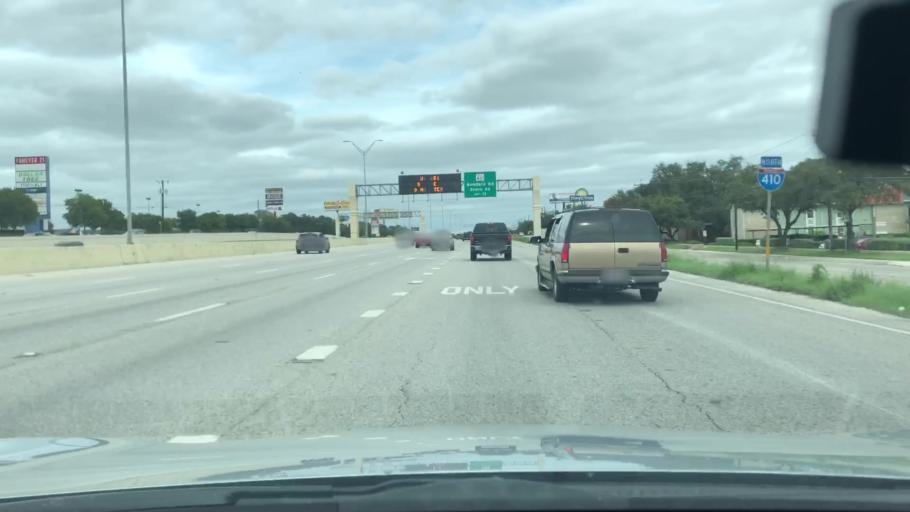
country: US
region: Texas
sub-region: Bexar County
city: Leon Valley
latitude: 29.4729
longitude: -98.6123
